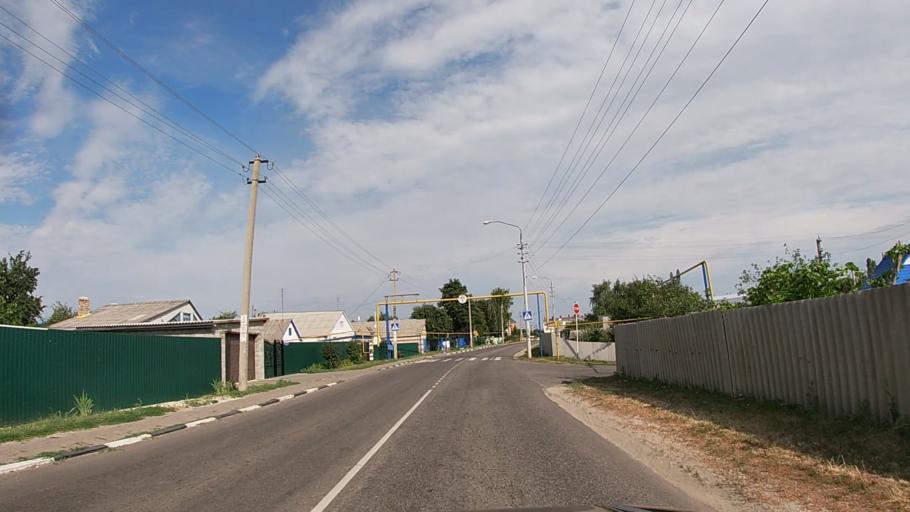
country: RU
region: Belgorod
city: Krasnaya Yaruga
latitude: 50.8004
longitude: 35.6613
